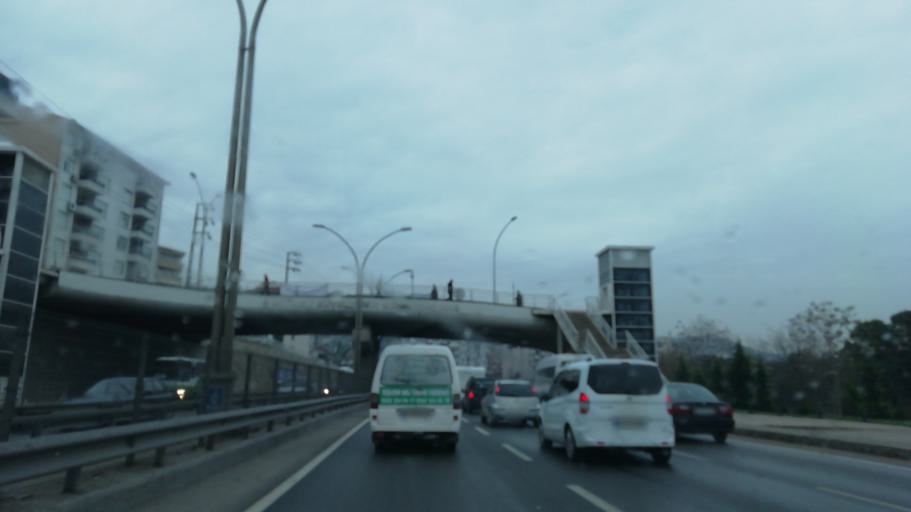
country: TR
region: Kocaeli
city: Izmit
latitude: 40.7658
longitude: 29.8989
